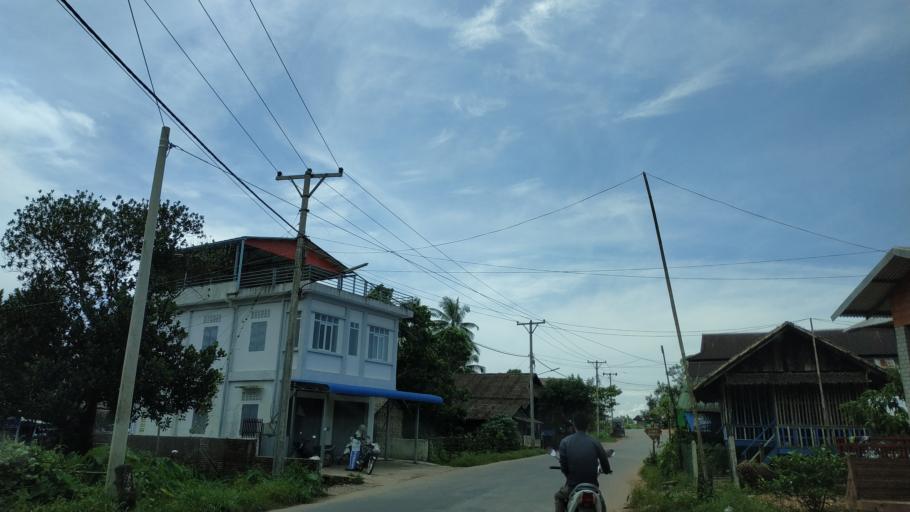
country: MM
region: Tanintharyi
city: Dawei
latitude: 14.1071
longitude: 98.1692
